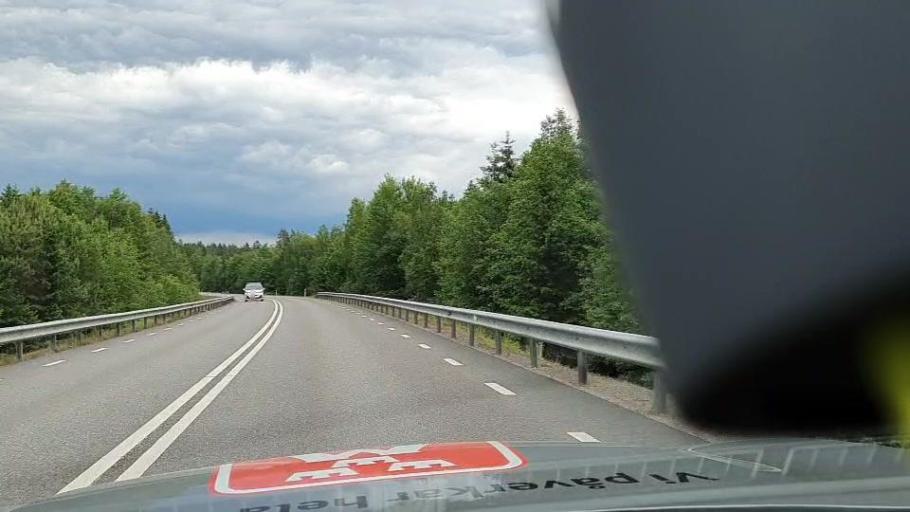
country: SE
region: Kalmar
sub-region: Emmaboda Kommun
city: Emmaboda
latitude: 56.4534
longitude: 15.5761
